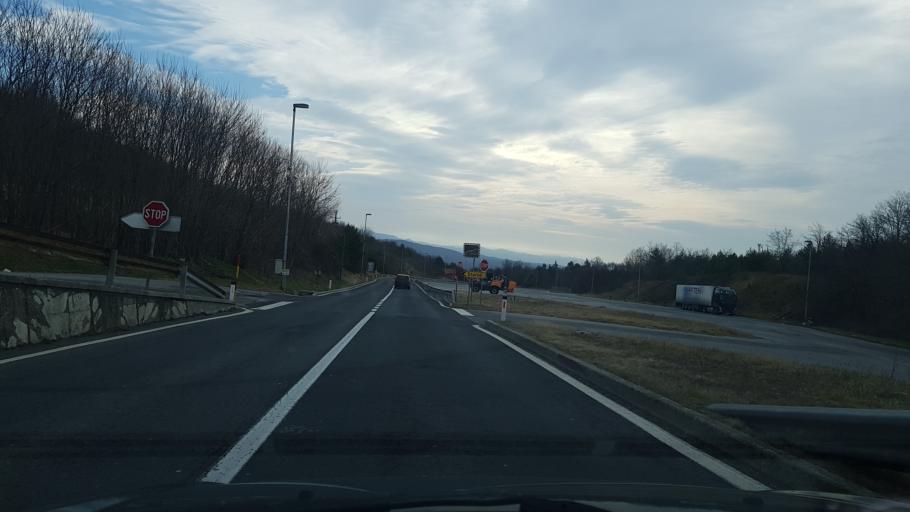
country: SI
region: Ilirska Bistrica
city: Ilirska Bistrica
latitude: 45.4935
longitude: 14.1989
